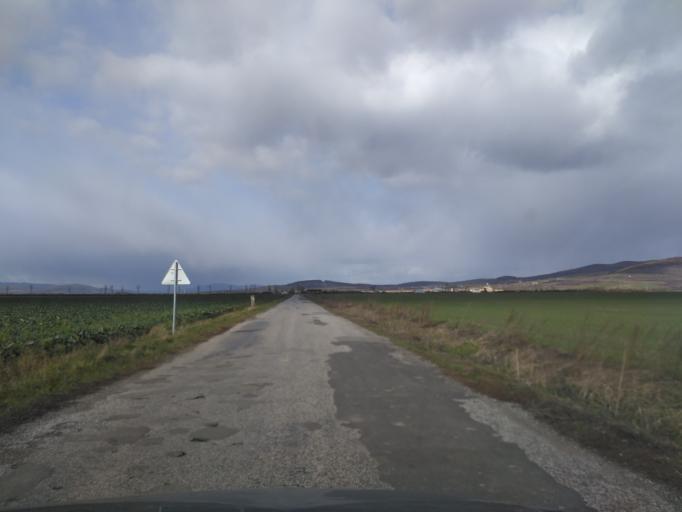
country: HU
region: Borsod-Abauj-Zemplen
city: Satoraljaujhely
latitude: 48.4136
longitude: 21.6796
